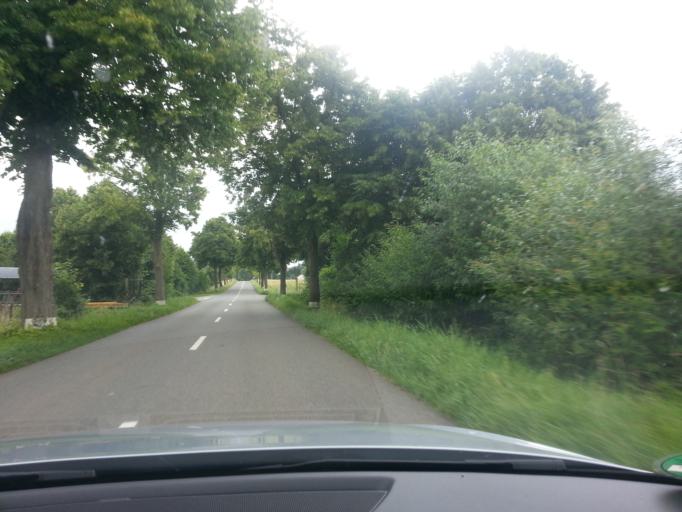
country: LU
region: Grevenmacher
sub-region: Canton de Remich
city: Mondorf-les-Bains
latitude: 49.5183
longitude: 6.2964
